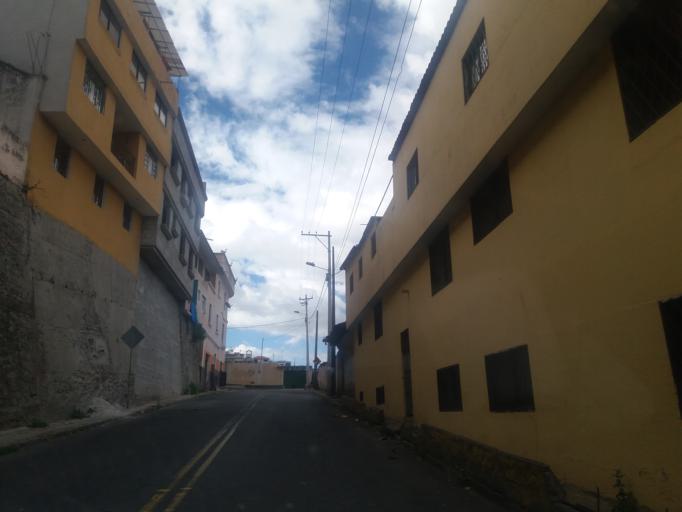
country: EC
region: Pichincha
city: Quito
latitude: -0.2197
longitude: -78.5232
